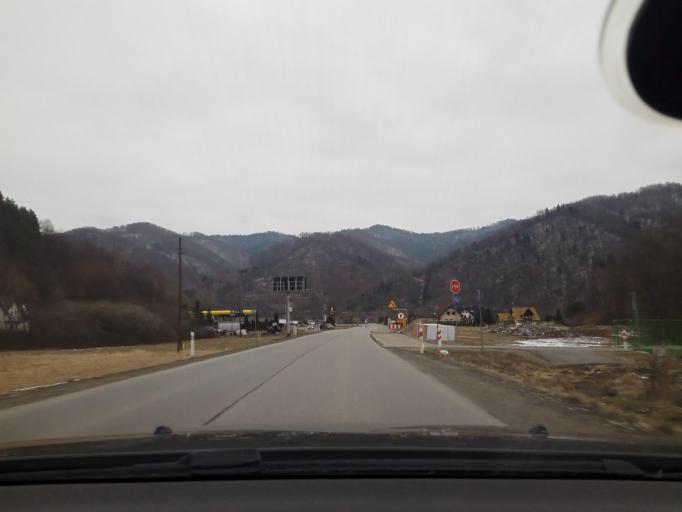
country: PL
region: Lesser Poland Voivodeship
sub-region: Powiat nowosadecki
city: Lacko
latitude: 49.5167
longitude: 20.4090
